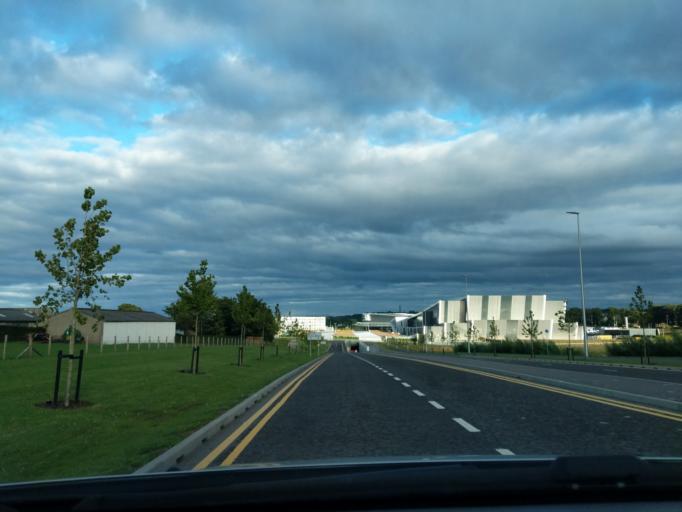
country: GB
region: Scotland
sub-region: Aberdeen City
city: Dyce
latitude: 57.1890
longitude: -2.1977
